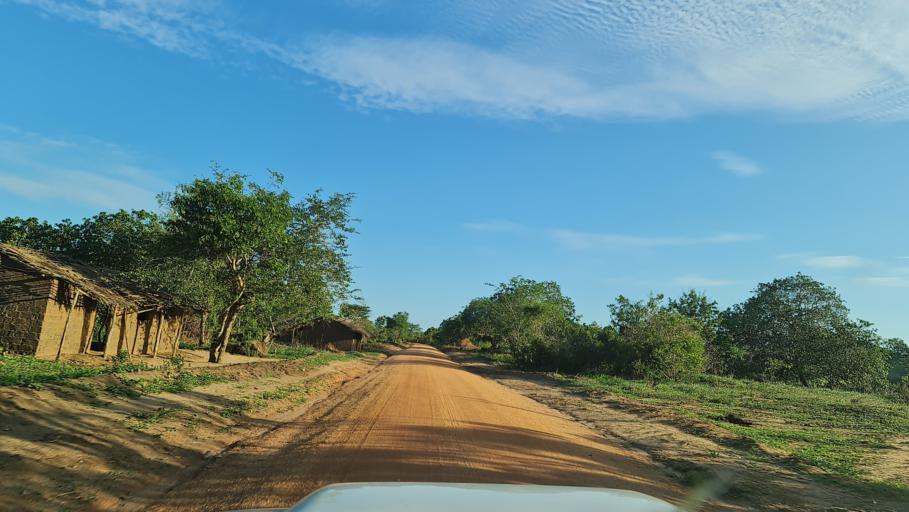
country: MZ
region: Nampula
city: Nacala
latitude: -14.6780
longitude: 40.2942
